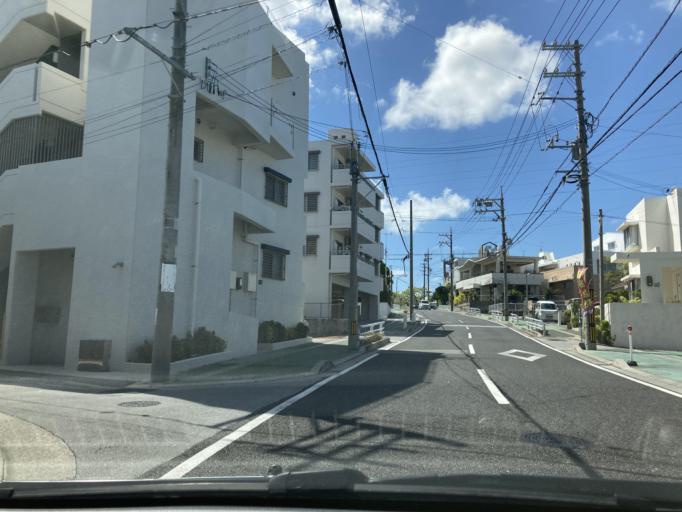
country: JP
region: Okinawa
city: Tomigusuku
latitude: 26.1953
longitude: 127.6711
